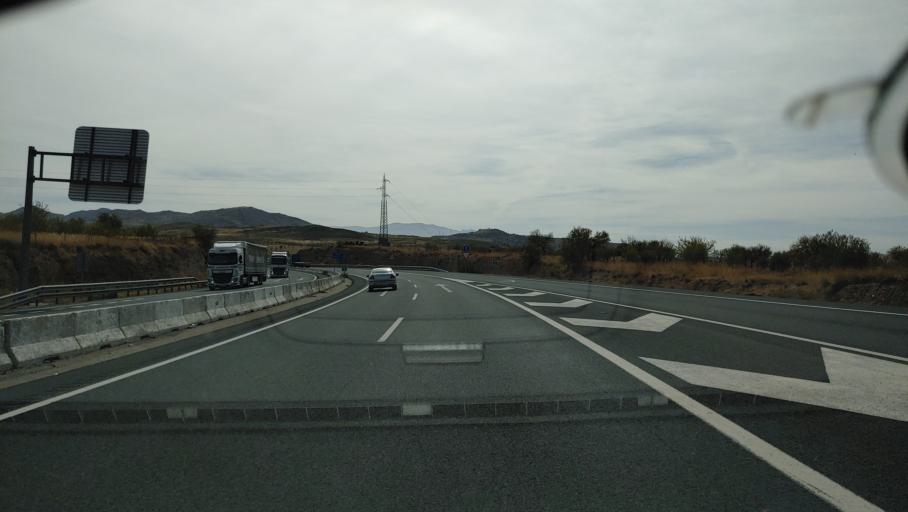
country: ES
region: Andalusia
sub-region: Provincia de Granada
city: Gor
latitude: 37.3969
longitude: -2.9924
